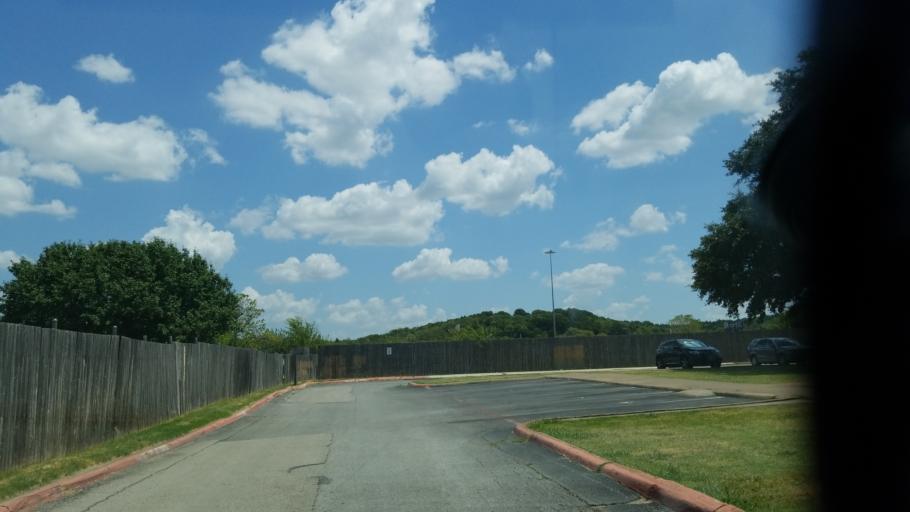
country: US
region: Texas
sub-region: Dallas County
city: Cockrell Hill
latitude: 32.7359
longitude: -96.9231
